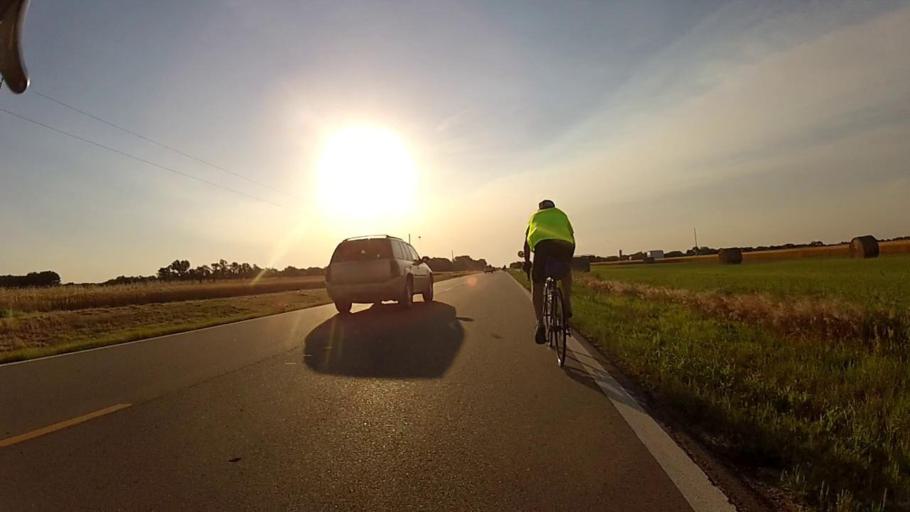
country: US
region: Kansas
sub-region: Harper County
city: Anthony
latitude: 37.1539
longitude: -97.8439
